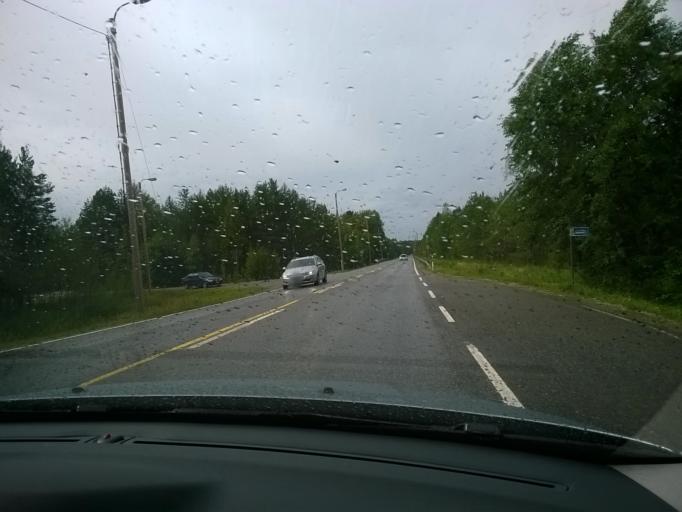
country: FI
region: Kainuu
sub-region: Kehys-Kainuu
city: Kuhmo
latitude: 64.1188
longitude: 29.5688
